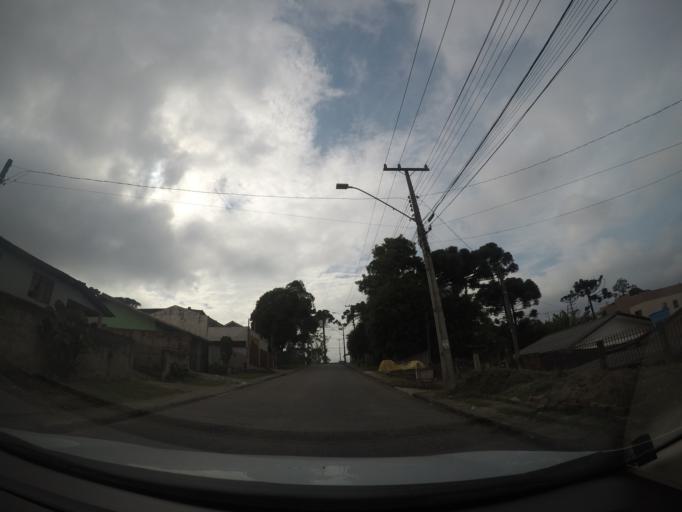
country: BR
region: Parana
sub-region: Colombo
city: Colombo
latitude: -25.3548
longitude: -49.2015
